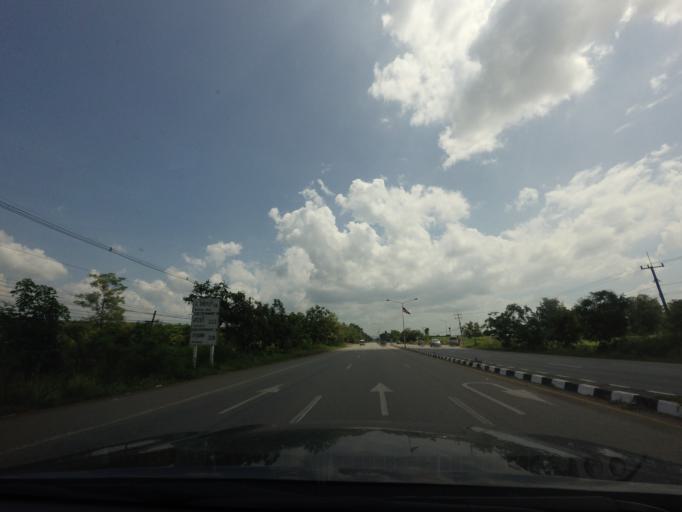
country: TH
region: Phetchabun
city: Phetchabun
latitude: 16.2467
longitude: 101.0720
